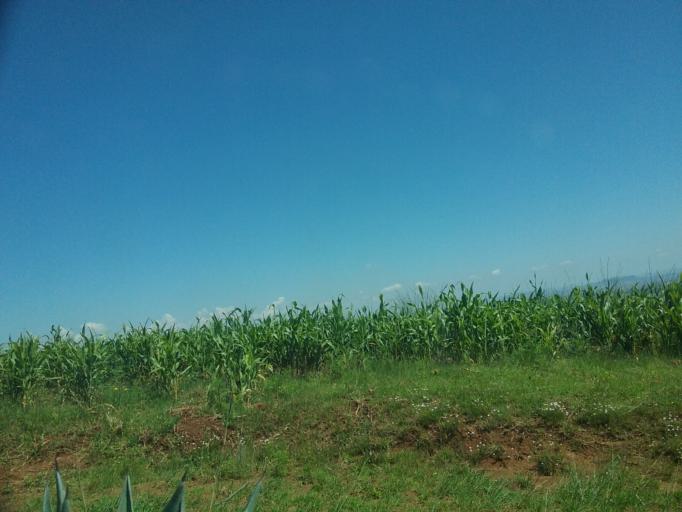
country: LS
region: Berea
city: Teyateyaneng
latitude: -29.2157
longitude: 27.8679
